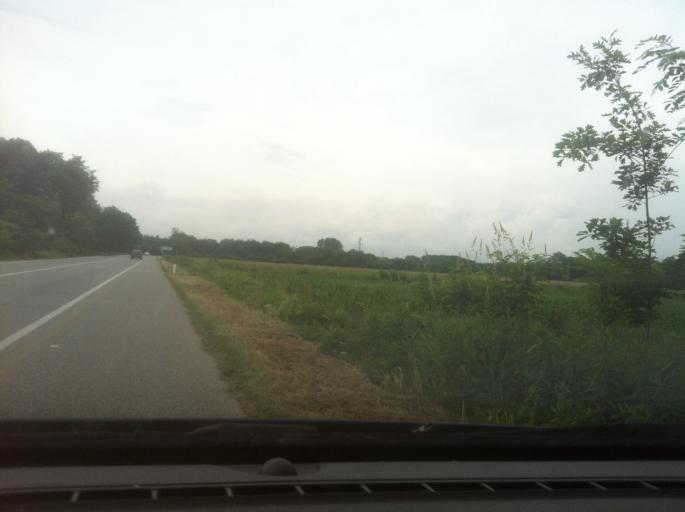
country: IT
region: Piedmont
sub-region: Provincia di Torino
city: Brandizzo
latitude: 45.2059
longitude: 7.8303
